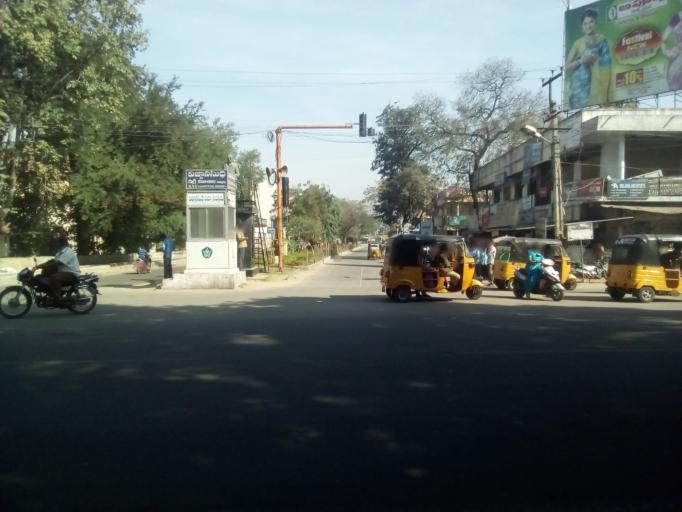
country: IN
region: Andhra Pradesh
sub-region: Chittoor
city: Chittoor
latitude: 13.2165
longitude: 79.1060
